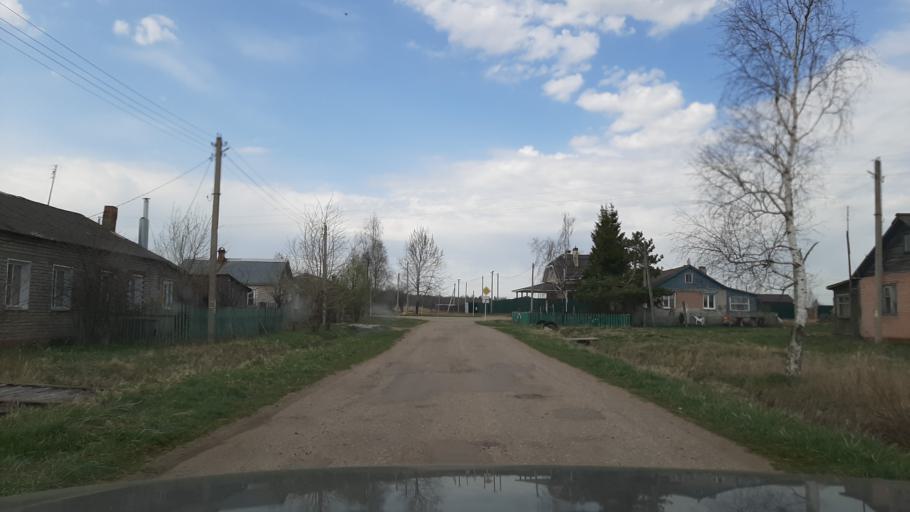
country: RU
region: Ivanovo
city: Furmanov
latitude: 57.3192
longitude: 41.1583
